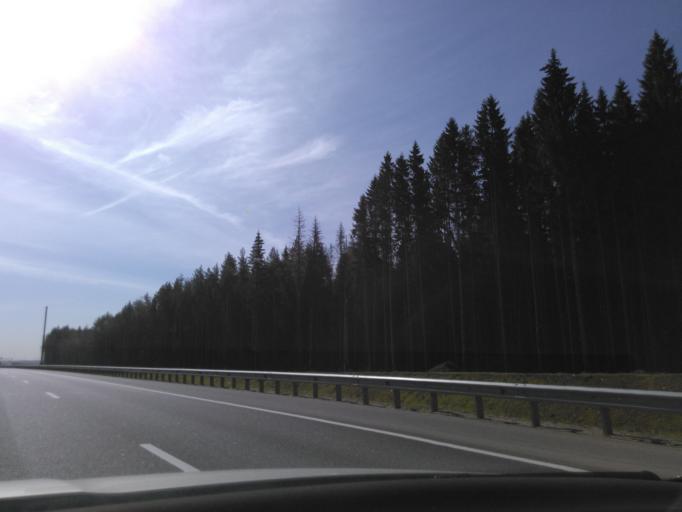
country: RU
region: Moskovskaya
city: Novopodrezkovo
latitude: 55.9685
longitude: 37.3374
